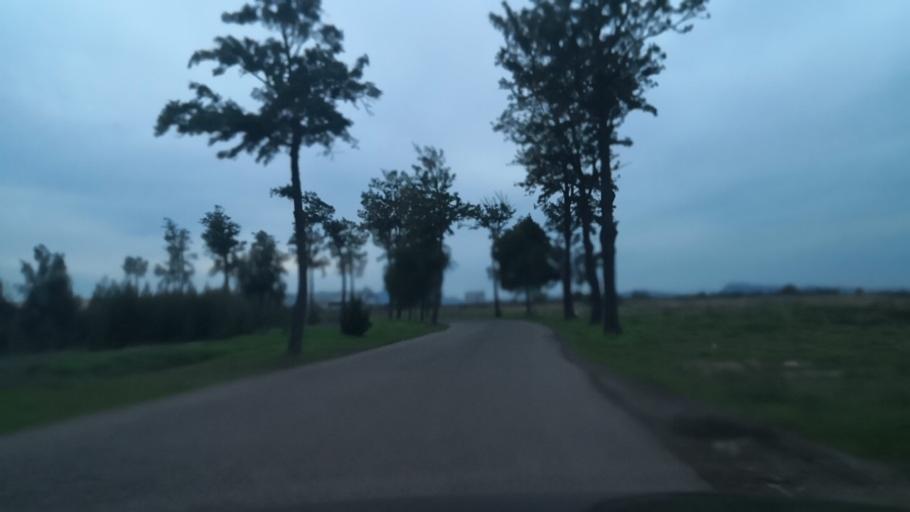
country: PT
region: Setubal
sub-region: Setubal
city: Setubal
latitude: 38.4975
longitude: -8.8213
